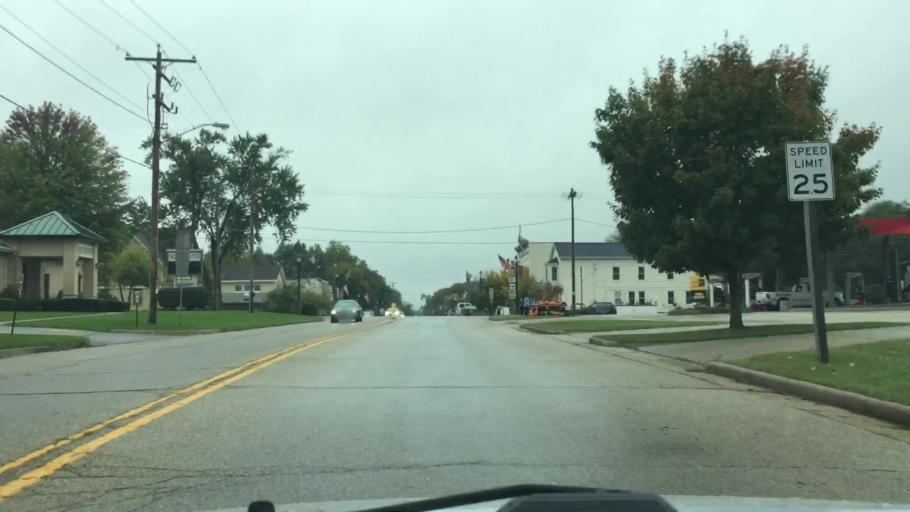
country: US
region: Wisconsin
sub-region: Jefferson County
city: Palmyra
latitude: 42.8792
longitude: -88.5839
